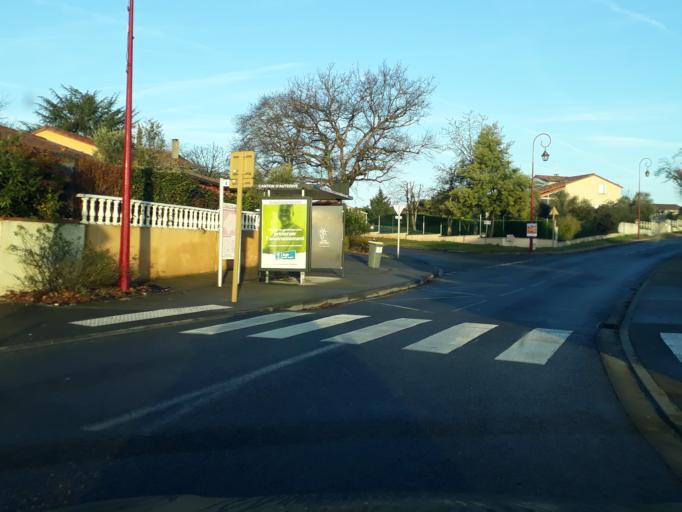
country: FR
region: Midi-Pyrenees
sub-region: Departement de la Haute-Garonne
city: Longages
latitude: 43.3535
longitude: 1.2368
